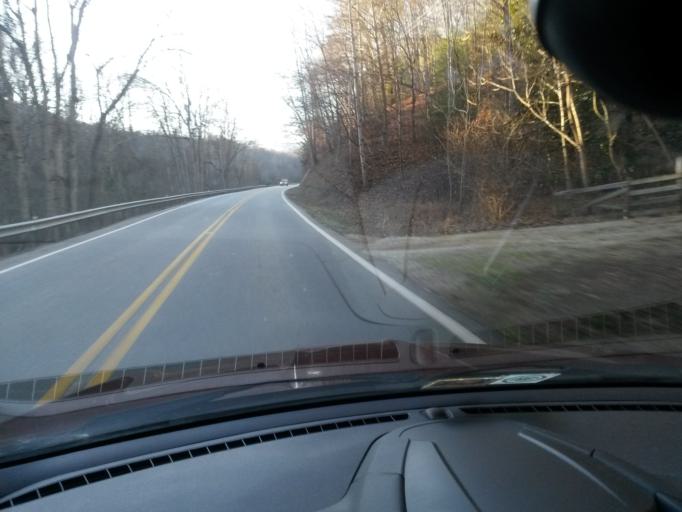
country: US
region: Virginia
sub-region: Amherst County
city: Amherst
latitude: 37.6375
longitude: -79.1181
